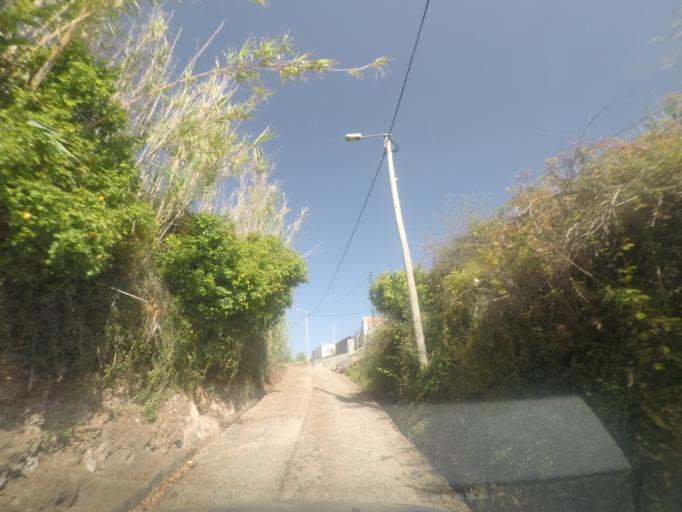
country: PT
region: Madeira
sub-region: Calheta
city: Faja da Ovelha
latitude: 32.8074
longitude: -17.2465
